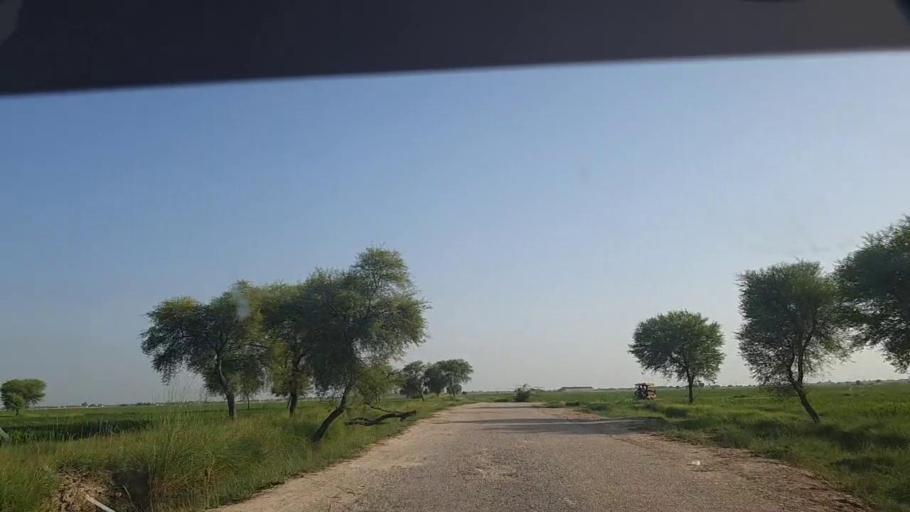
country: PK
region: Sindh
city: Tangwani
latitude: 28.2606
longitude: 69.0137
